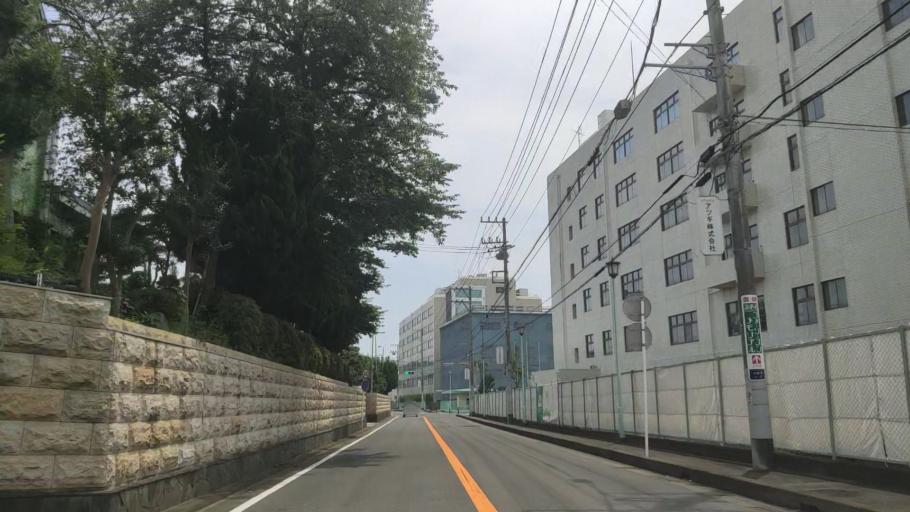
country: JP
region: Kanagawa
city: Atsugi
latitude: 35.4443
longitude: 139.3952
